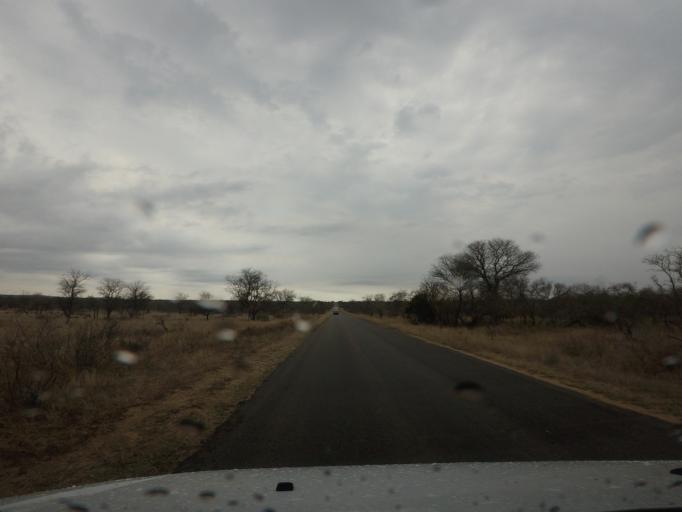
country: ZA
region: Limpopo
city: Thulamahashi
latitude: -24.4731
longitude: 31.4107
